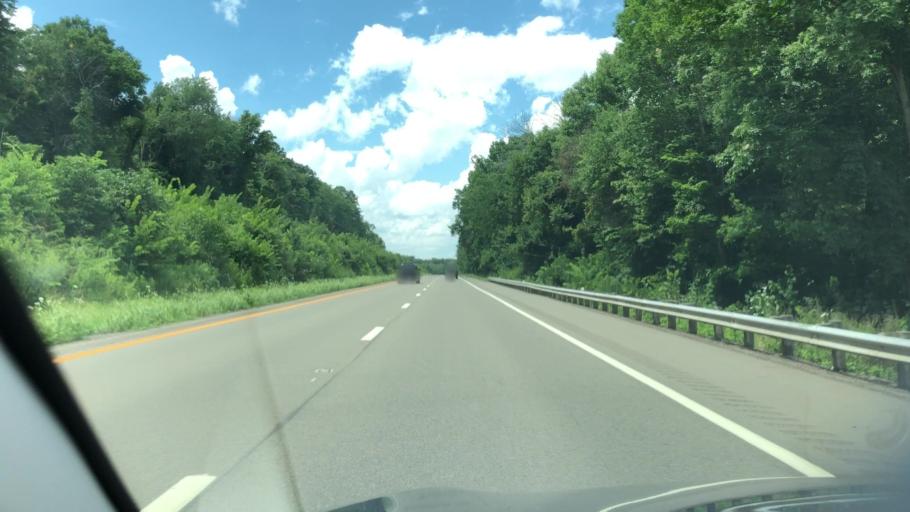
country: US
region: Ohio
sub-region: Stark County
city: Canal Fulton
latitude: 40.8503
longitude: -81.5644
